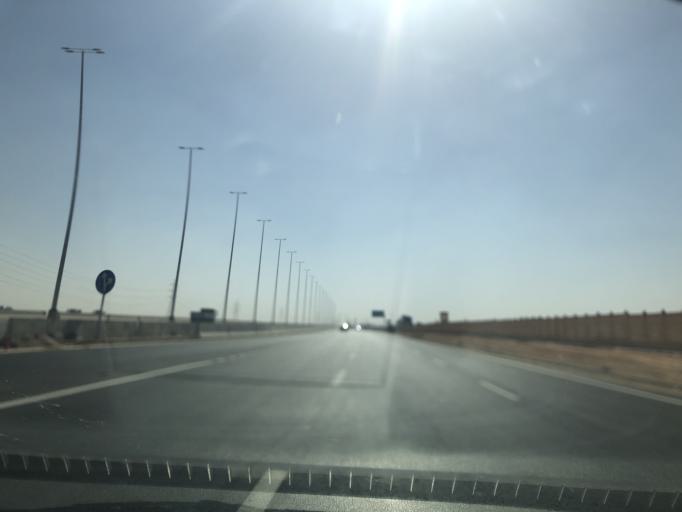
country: EG
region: Al Jizah
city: Madinat Sittah Uktubar
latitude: 29.8861
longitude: 31.0791
